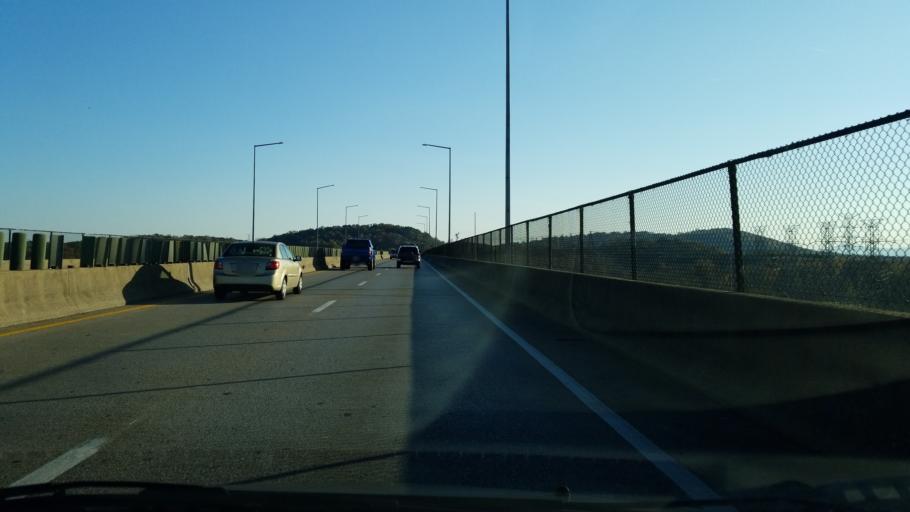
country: US
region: Tennessee
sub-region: Hamilton County
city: East Chattanooga
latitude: 35.1037
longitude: -85.2292
